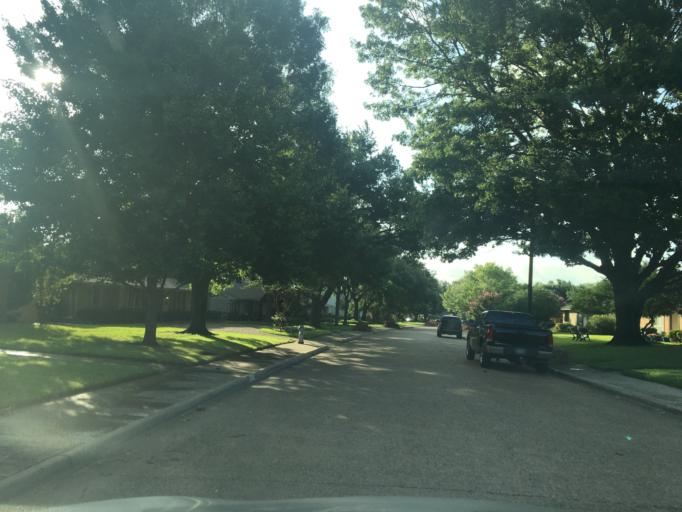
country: US
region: Texas
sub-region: Dallas County
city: Highland Park
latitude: 32.8477
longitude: -96.7558
